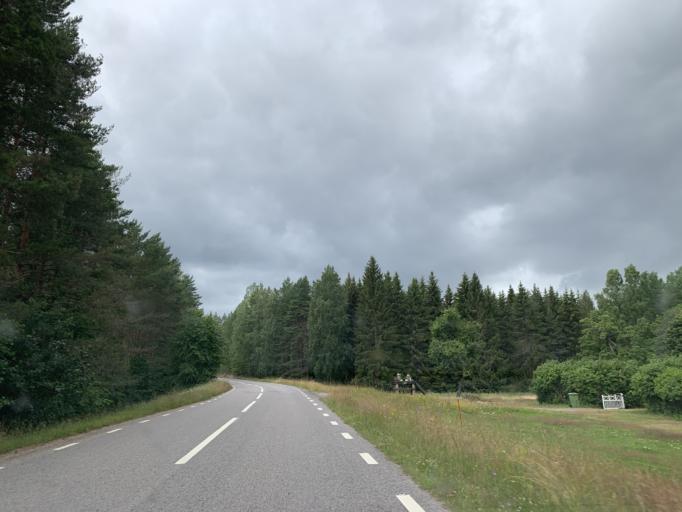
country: SE
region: Kalmar
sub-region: Vasterviks Kommun
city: Overum
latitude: 58.0241
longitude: 16.1191
